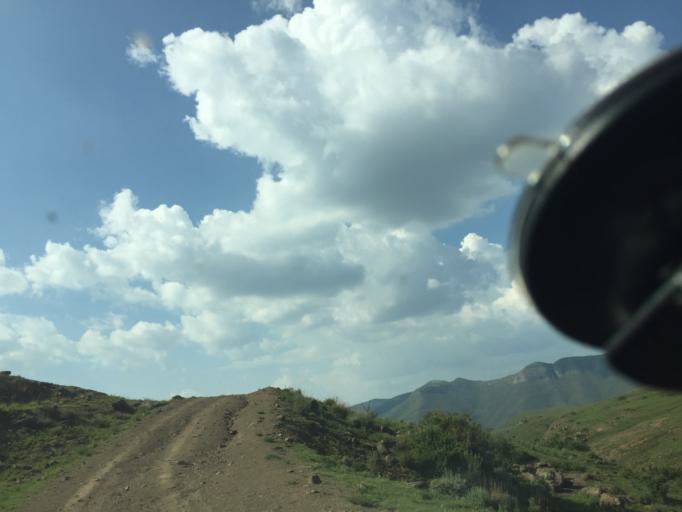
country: LS
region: Maseru
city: Nako
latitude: -29.6332
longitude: 28.1070
